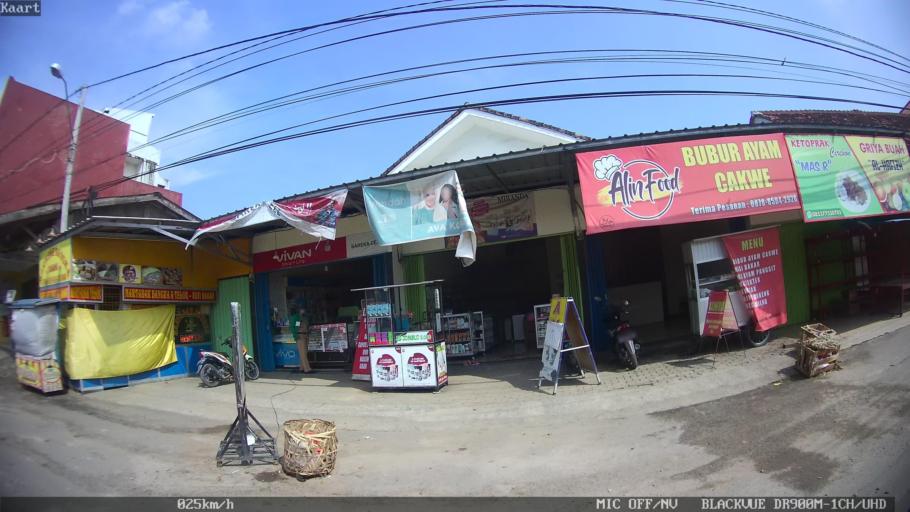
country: ID
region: Lampung
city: Kedaton
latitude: -5.3590
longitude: 105.2581
